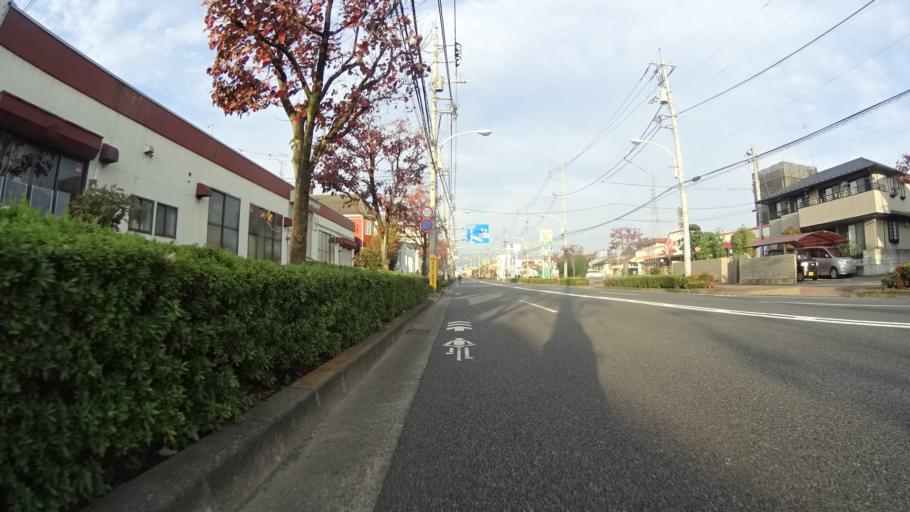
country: JP
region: Tokyo
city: Fussa
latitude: 35.7248
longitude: 139.2774
